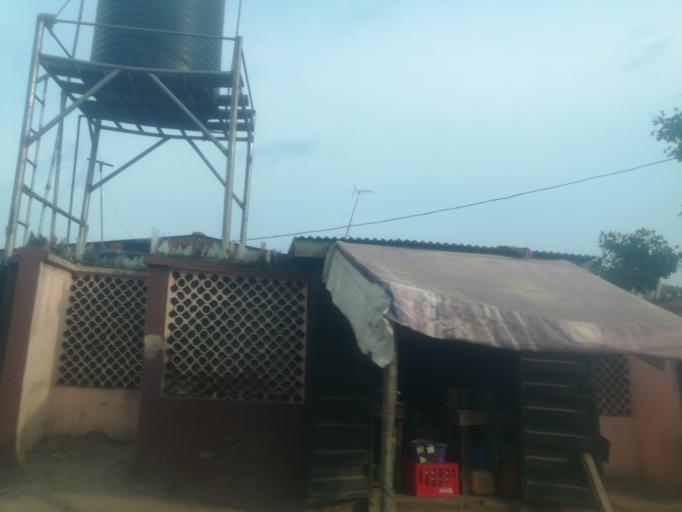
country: NG
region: Ogun
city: Abeokuta
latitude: 7.1622
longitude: 3.3130
